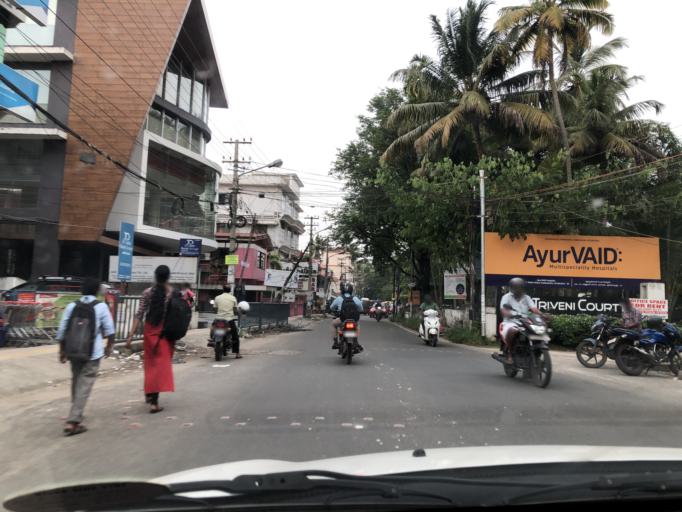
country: IN
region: Kerala
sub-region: Ernakulam
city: Cochin
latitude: 9.9630
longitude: 76.3007
